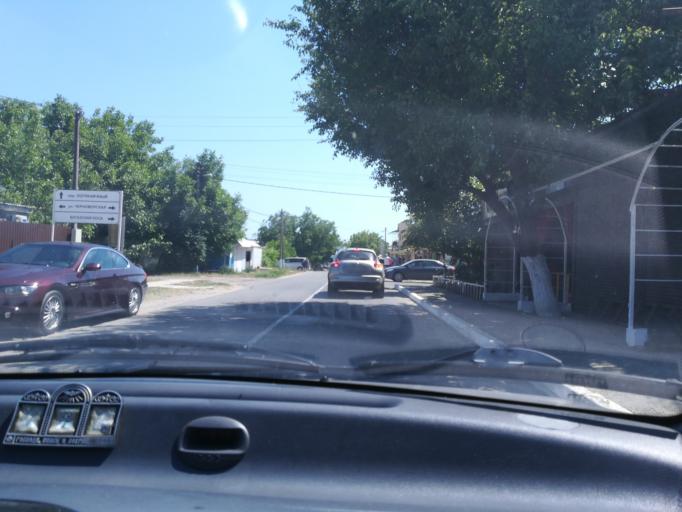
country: RU
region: Krasnodarskiy
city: Blagovetschenskaya
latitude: 45.0550
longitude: 37.1203
